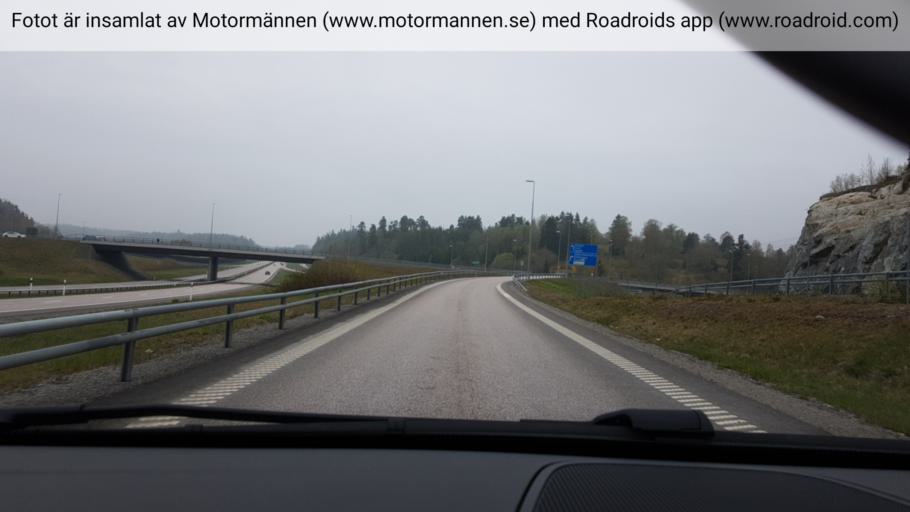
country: SE
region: Stockholm
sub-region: Nynashamns Kommun
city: Osmo
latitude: 58.9792
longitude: 17.9139
